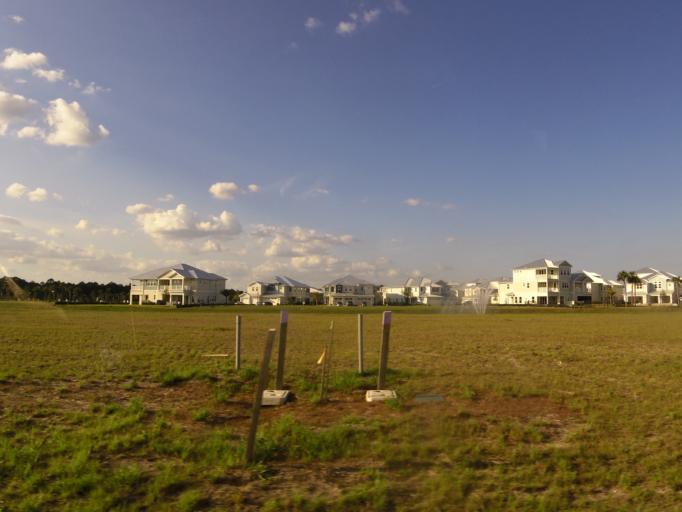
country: US
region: Florida
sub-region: Saint Johns County
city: Palm Valley
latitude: 30.0798
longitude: -81.4850
